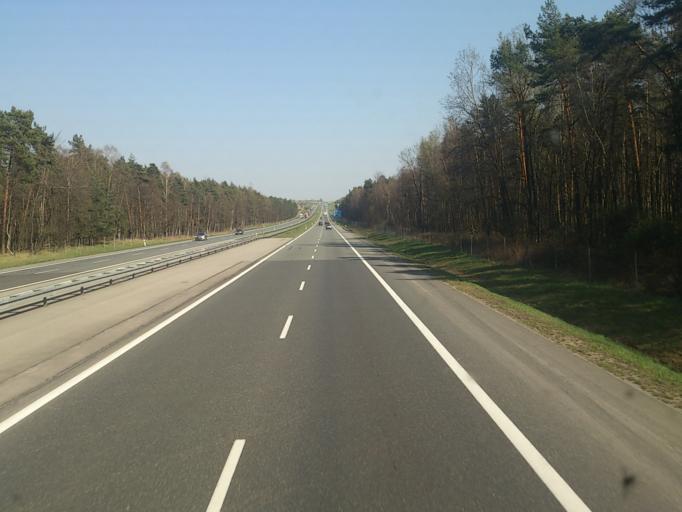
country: PL
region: Lesser Poland Voivodeship
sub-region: Powiat chrzanowski
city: Regulice
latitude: 50.1049
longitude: 19.5270
